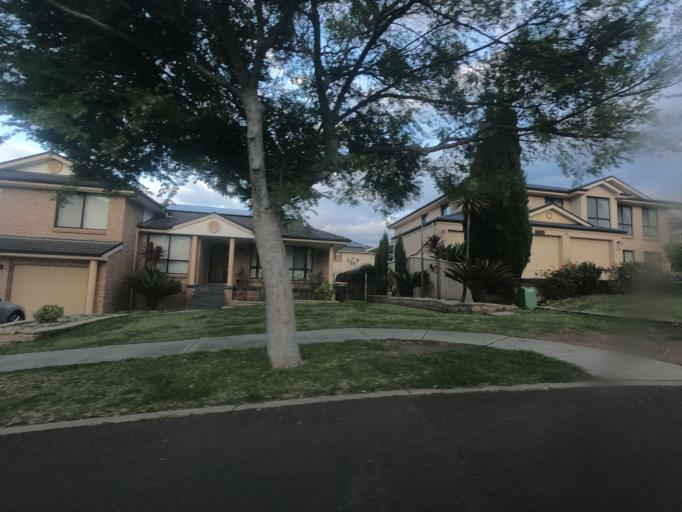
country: AU
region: New South Wales
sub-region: Wollongong
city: Dapto
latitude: -34.4939
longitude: 150.7743
